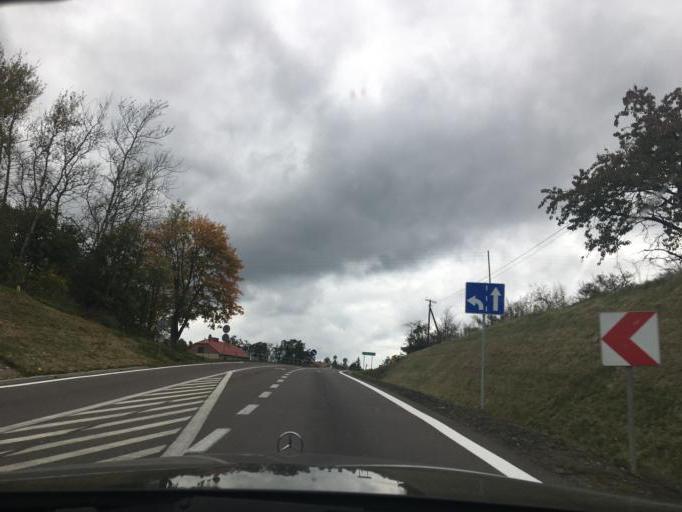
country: PL
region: Subcarpathian Voivodeship
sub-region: Powiat brzozowski
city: Jablonica Polska
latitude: 49.7179
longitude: 21.9008
